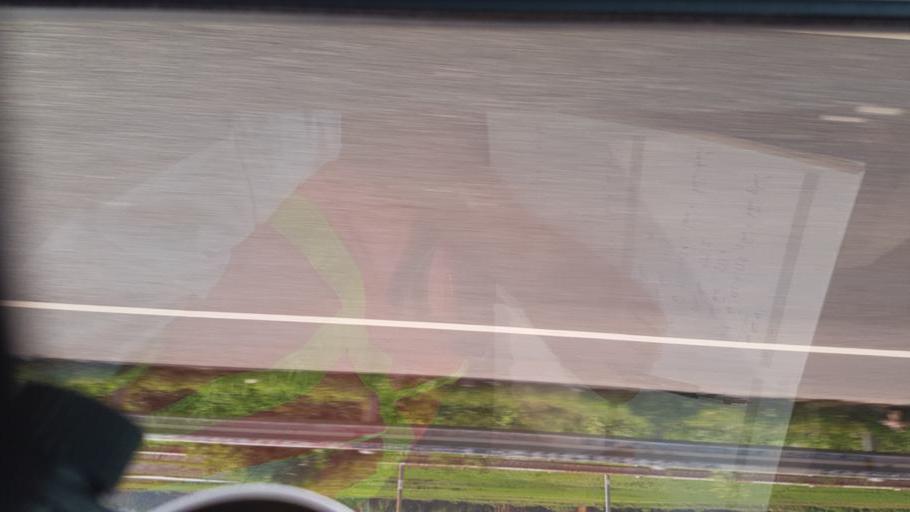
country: VN
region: Bac Giang
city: Bac Giang
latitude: 21.2489
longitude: 106.1596
